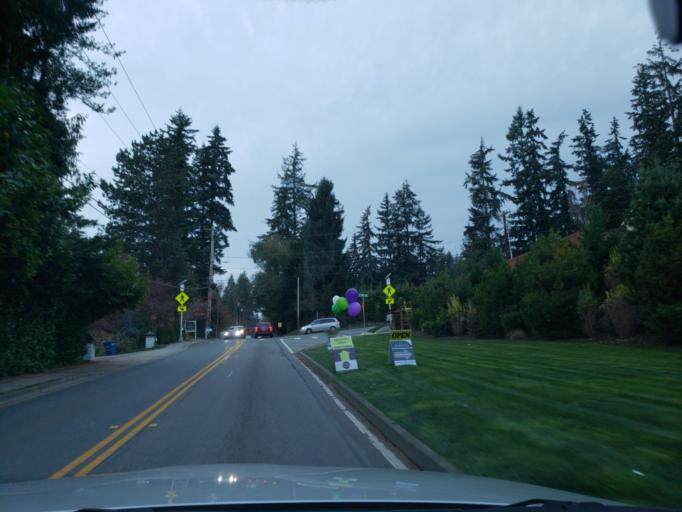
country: US
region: Washington
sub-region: King County
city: Bothell
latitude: 47.7803
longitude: -122.2268
